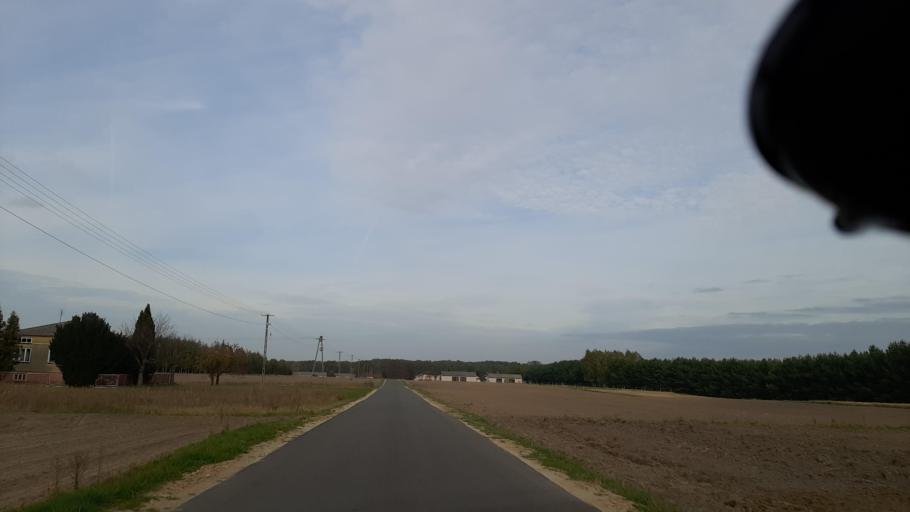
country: PL
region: Lublin Voivodeship
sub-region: Powiat lubelski
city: Garbow
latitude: 51.3971
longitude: 22.3519
